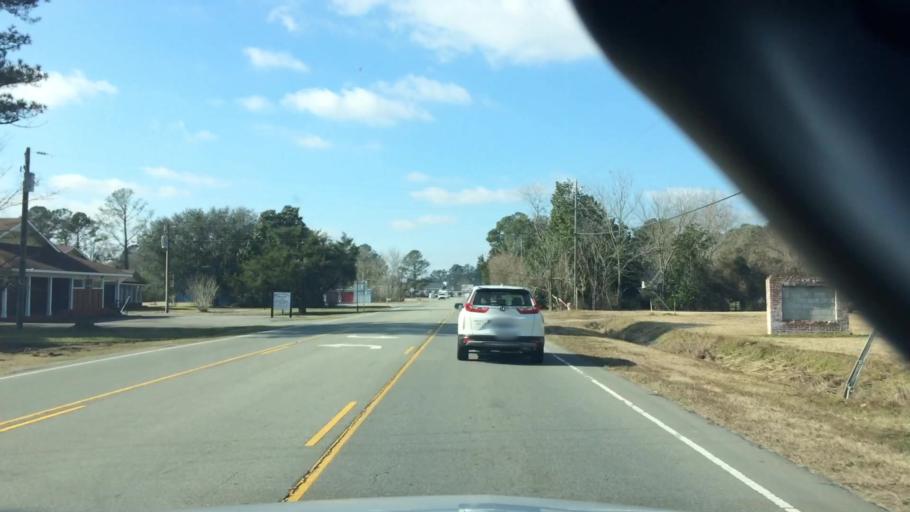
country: US
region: North Carolina
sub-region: Duplin County
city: Beulaville
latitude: 34.8300
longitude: -77.8138
